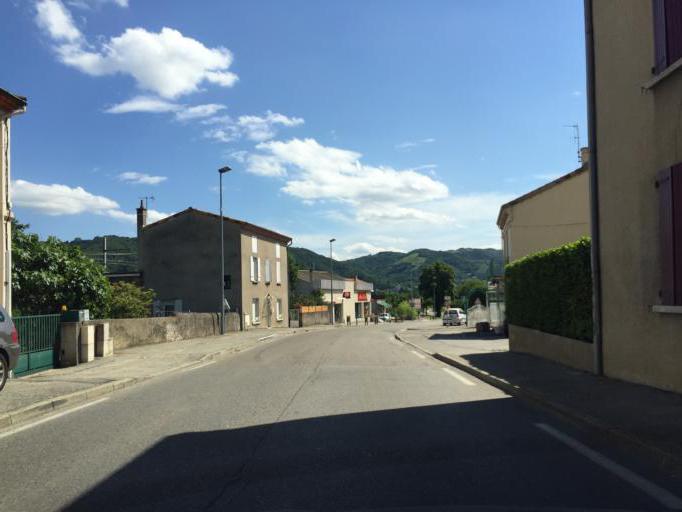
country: FR
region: Rhone-Alpes
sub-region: Departement de l'Ardeche
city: Saint-Jean-de-Muzols
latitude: 45.0812
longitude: 4.8144
